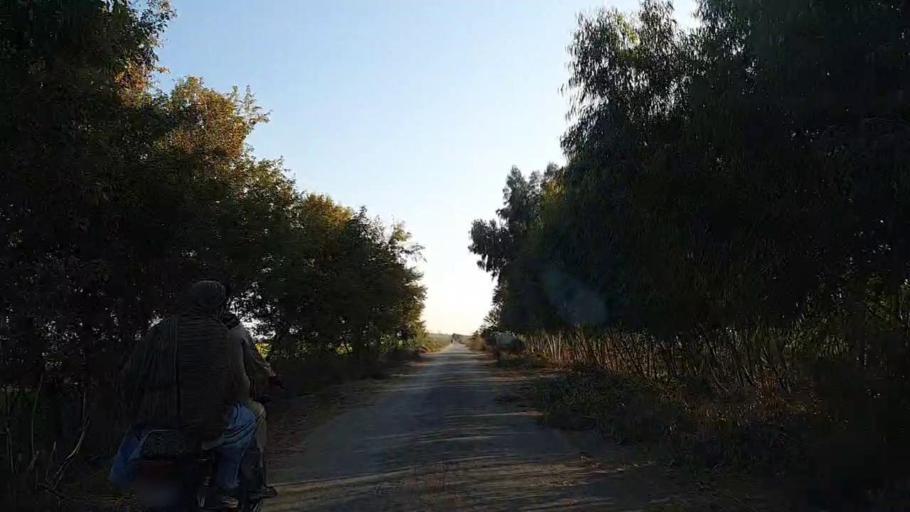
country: PK
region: Sindh
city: Khadro
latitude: 26.2739
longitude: 68.8100
